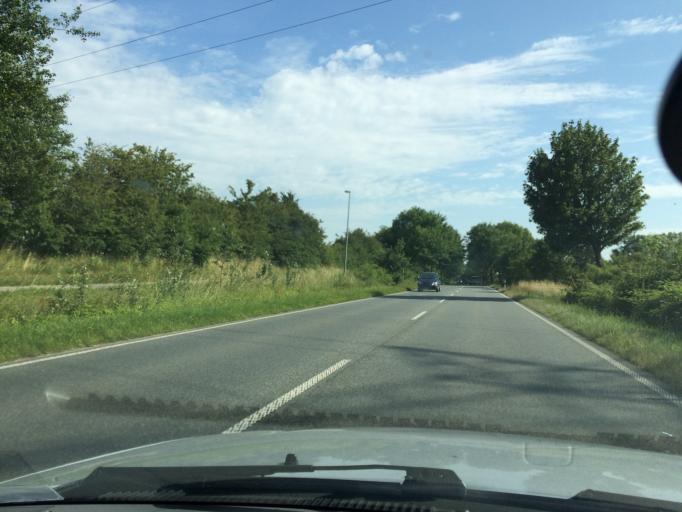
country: DE
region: Schleswig-Holstein
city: Jarplund-Weding
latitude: 54.7504
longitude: 9.4363
